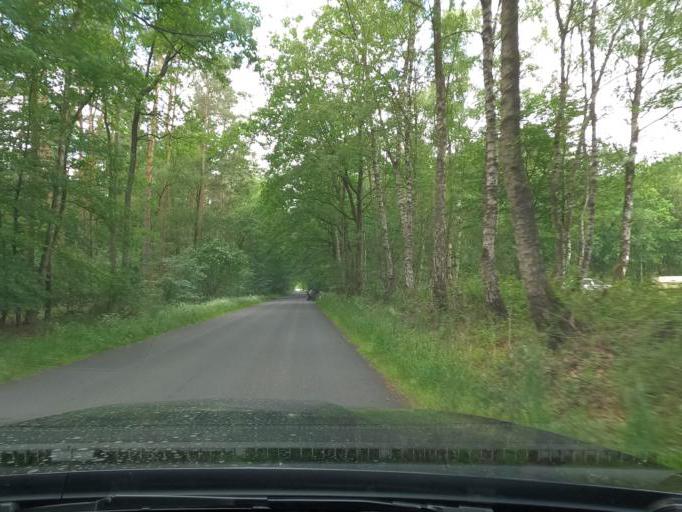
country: DE
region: Lower Saxony
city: Steimbke
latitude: 52.6379
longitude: 9.4652
